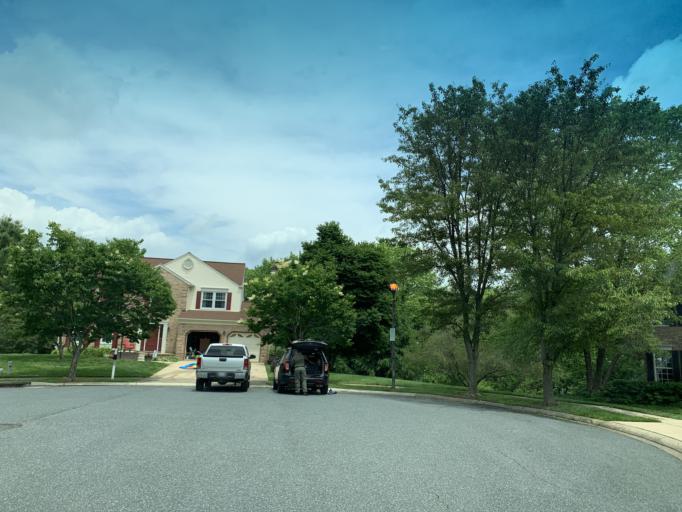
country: US
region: Maryland
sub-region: Harford County
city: South Bel Air
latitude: 39.5604
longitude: -76.3339
